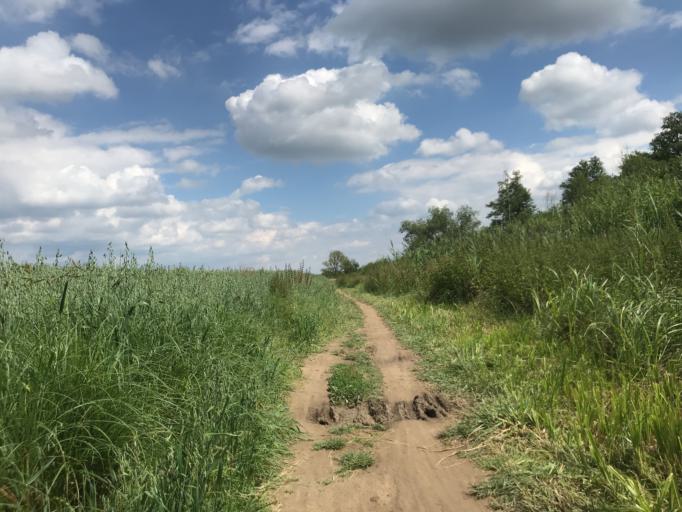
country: CZ
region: Jihocesky
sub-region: Okres Jindrichuv Hradec
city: Trebon
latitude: 48.9935
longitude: 14.7268
